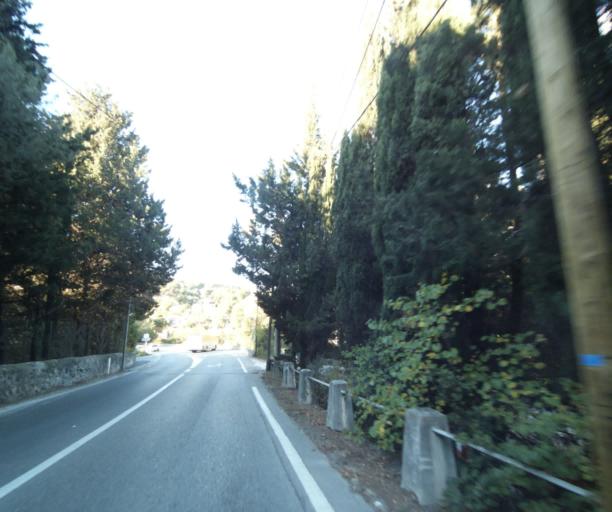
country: FR
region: Provence-Alpes-Cote d'Azur
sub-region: Departement des Bouches-du-Rhone
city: Cassis
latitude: 43.2163
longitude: 5.5507
